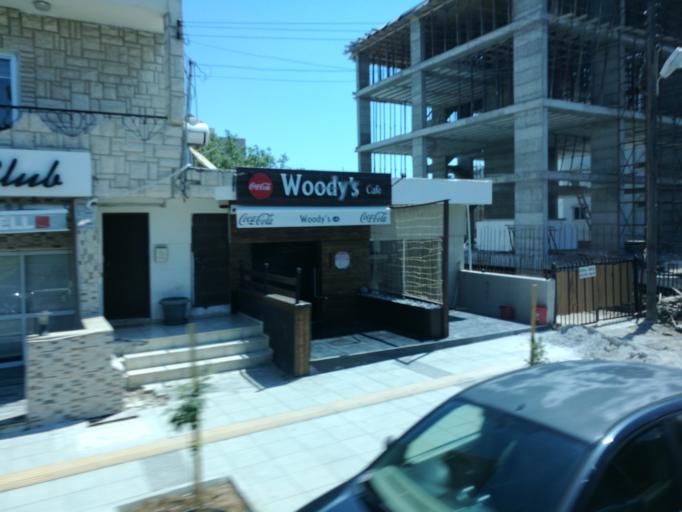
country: CY
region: Ammochostos
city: Famagusta
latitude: 35.1437
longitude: 33.9134
